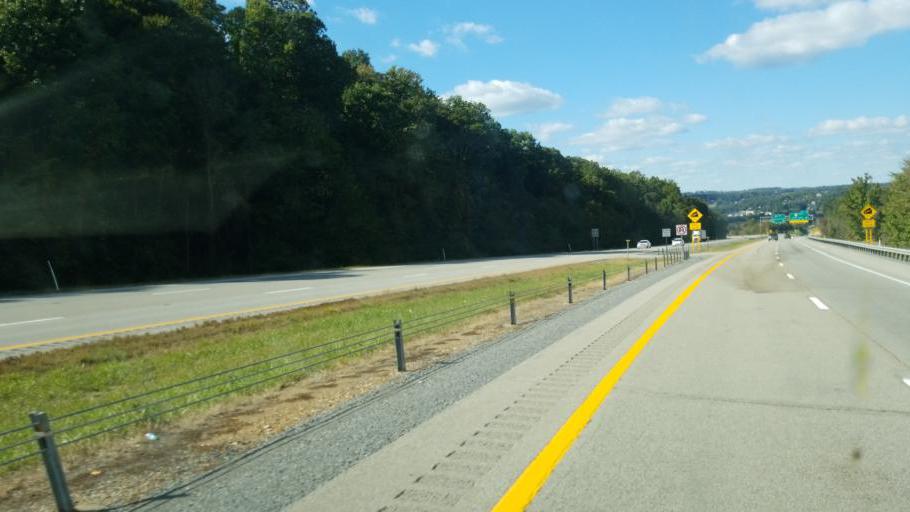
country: US
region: West Virginia
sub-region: Monongalia County
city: Cheat Lake
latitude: 39.6628
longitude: -79.8446
